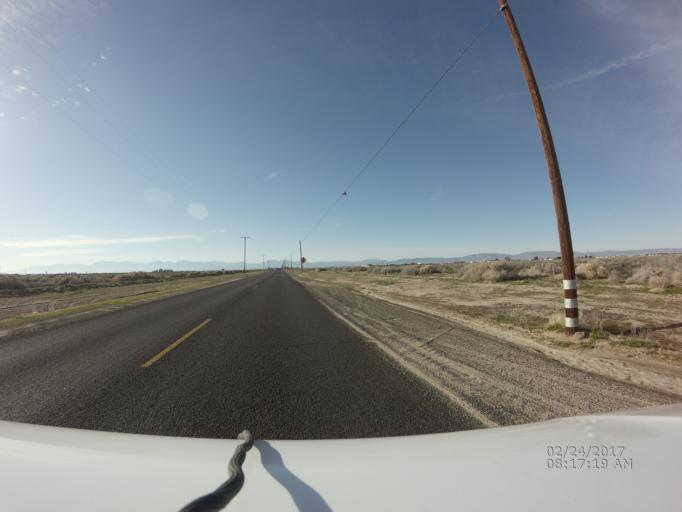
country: US
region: California
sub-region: Los Angeles County
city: Lancaster
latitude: 34.7217
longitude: -118.0412
